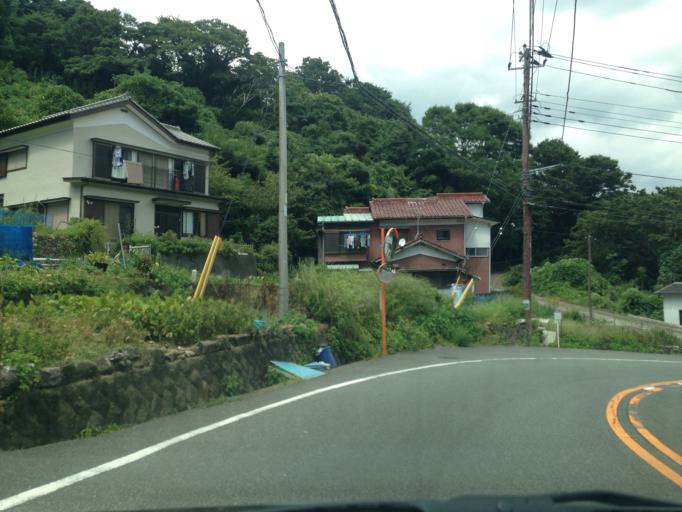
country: JP
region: Shizuoka
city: Shimoda
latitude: 34.6569
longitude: 138.7894
